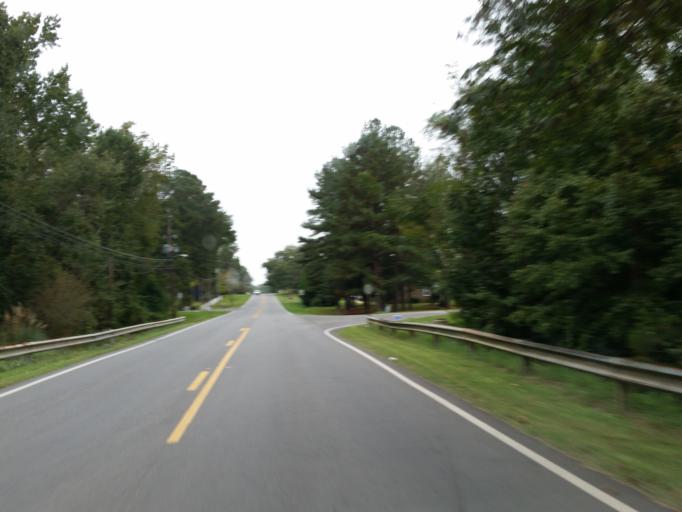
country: US
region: Georgia
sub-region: Dooly County
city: Unadilla
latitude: 32.2729
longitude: -83.7386
